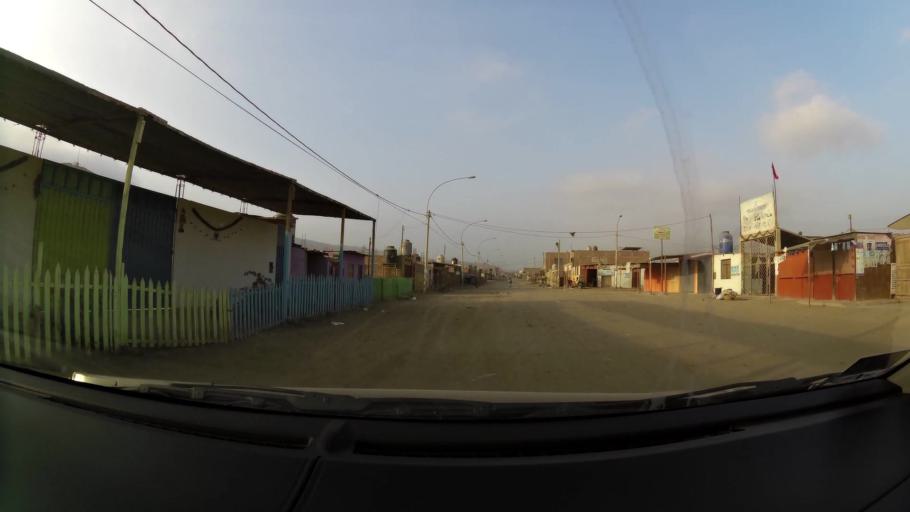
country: PE
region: Lima
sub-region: Lima
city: Santa Rosa
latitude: -11.7458
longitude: -77.1478
